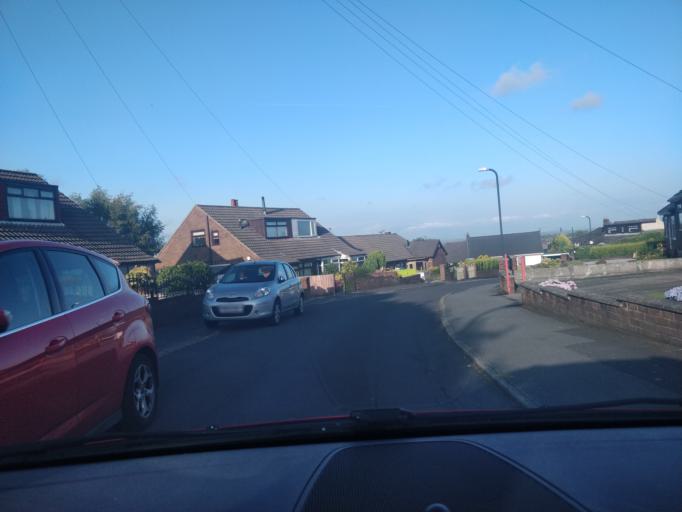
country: GB
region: England
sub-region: Lancashire
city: Appley Bridge
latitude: 53.5422
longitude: -2.7267
